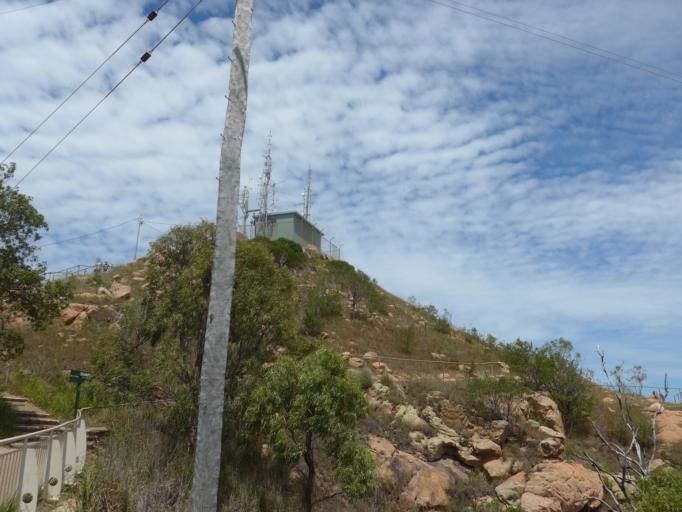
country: AU
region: Queensland
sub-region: Townsville
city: Townsville
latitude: -19.2583
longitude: 146.8033
